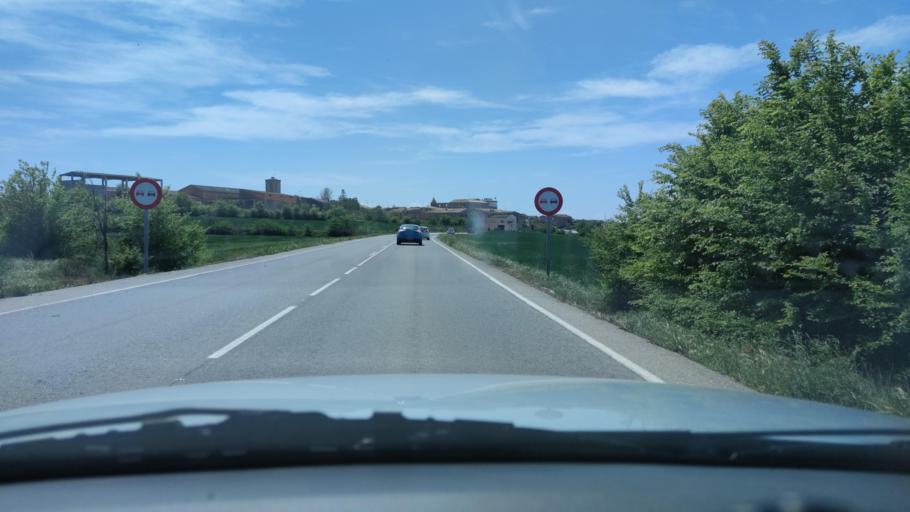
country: ES
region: Catalonia
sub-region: Provincia de Lleida
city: Mont-roig del Camp
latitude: 41.7543
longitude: 1.2386
